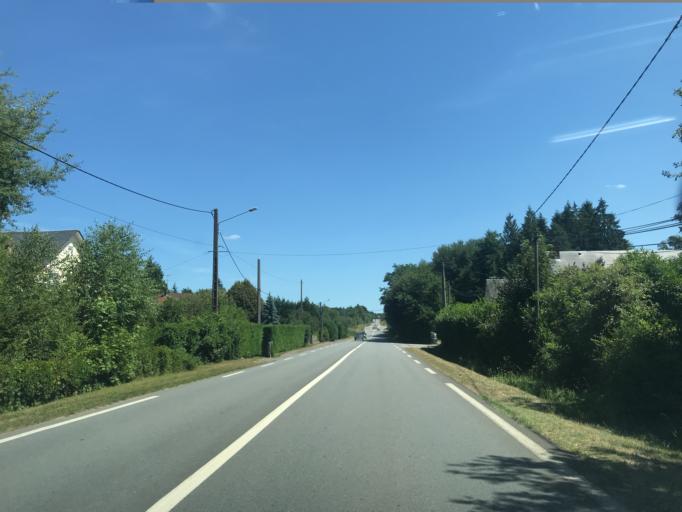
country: FR
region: Limousin
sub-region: Departement de la Correze
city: Correze
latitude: 45.3329
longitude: 1.8858
